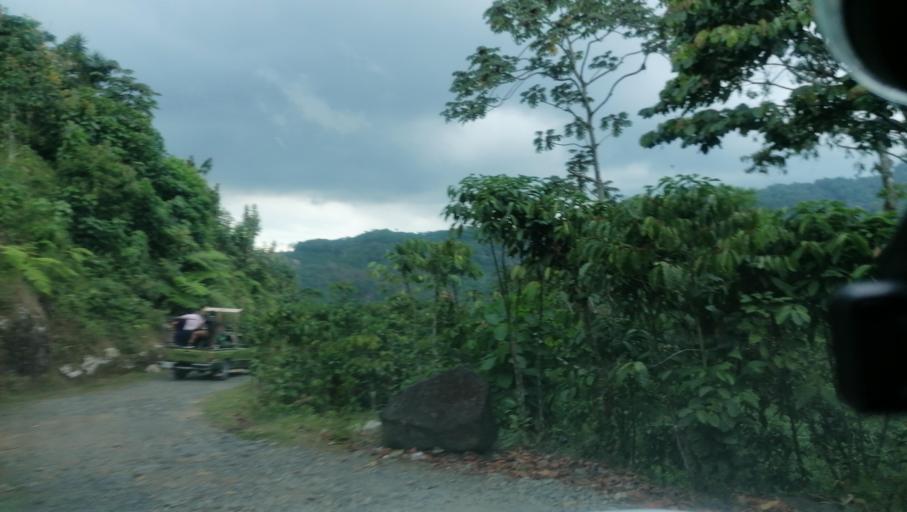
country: MX
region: Chiapas
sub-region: Cacahoatan
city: Benito Juarez
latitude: 15.0730
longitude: -92.1660
